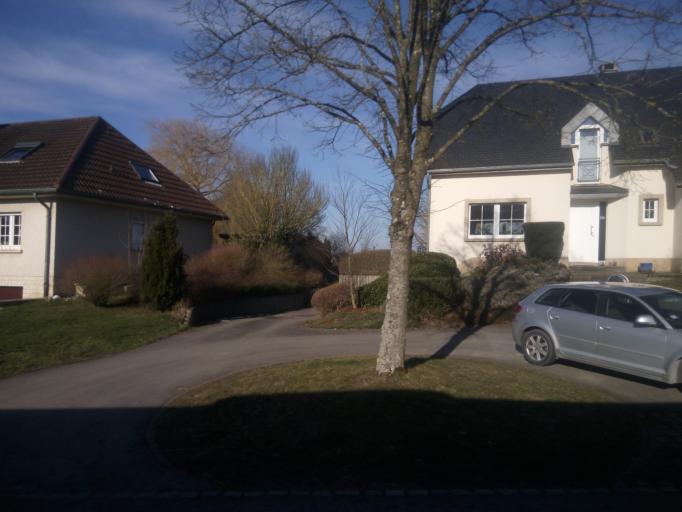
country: LU
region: Grevenmacher
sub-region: Canton d'Echternach
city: Berdorf
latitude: 49.8160
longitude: 6.3438
